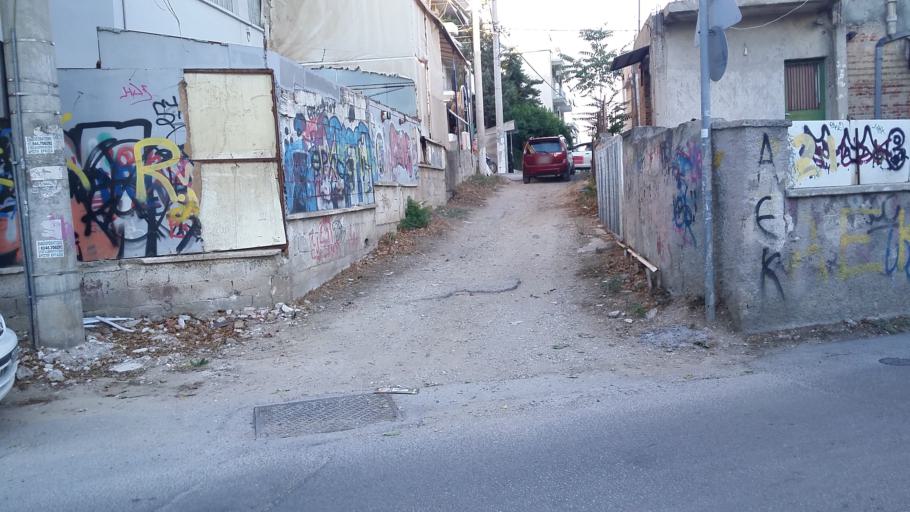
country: GR
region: Attica
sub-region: Nomarchia Athinas
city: Irakleio
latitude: 38.0528
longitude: 23.7592
